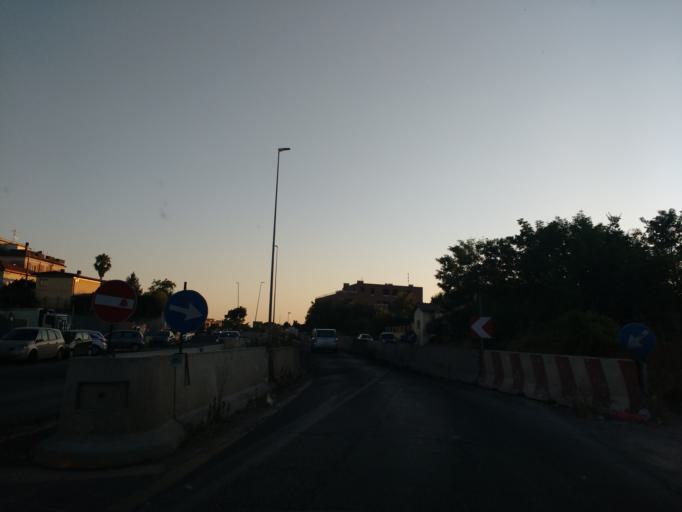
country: IT
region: Latium
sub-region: Citta metropolitana di Roma Capitale
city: Setteville
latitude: 41.9403
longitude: 12.6312
